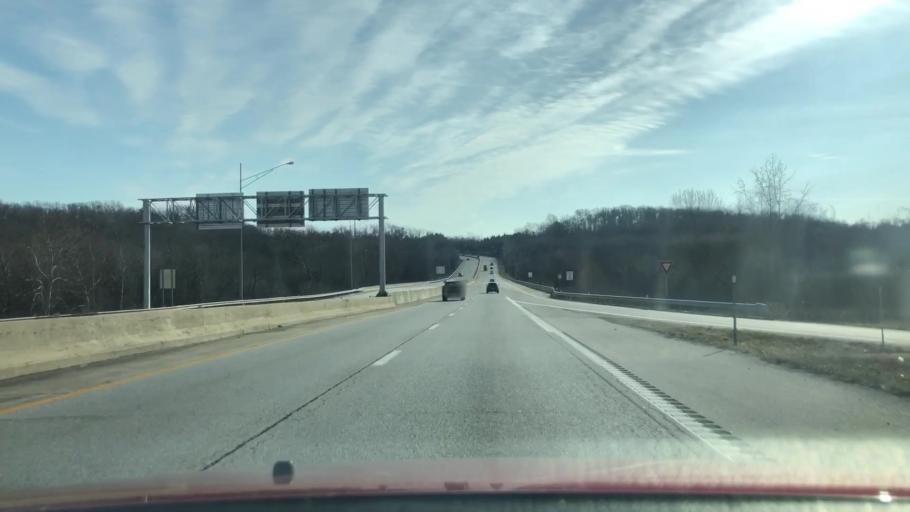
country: US
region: Missouri
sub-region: Christian County
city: Nixa
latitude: 37.1262
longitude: -93.2284
